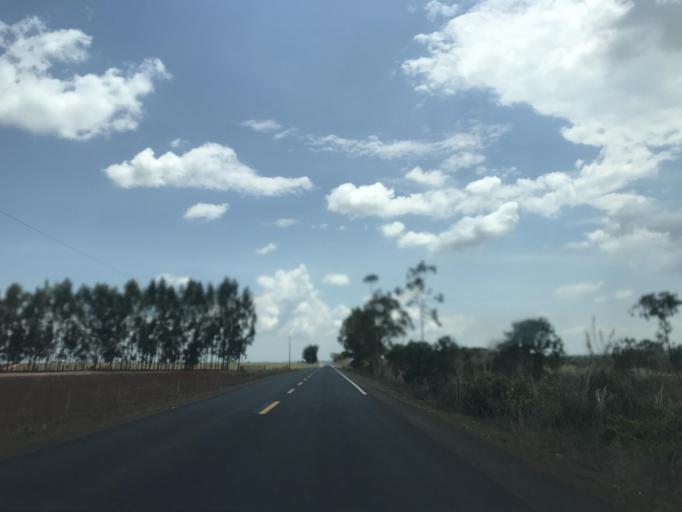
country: BR
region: Goias
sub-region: Bela Vista De Goias
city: Bela Vista de Goias
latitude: -17.0950
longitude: -48.6560
